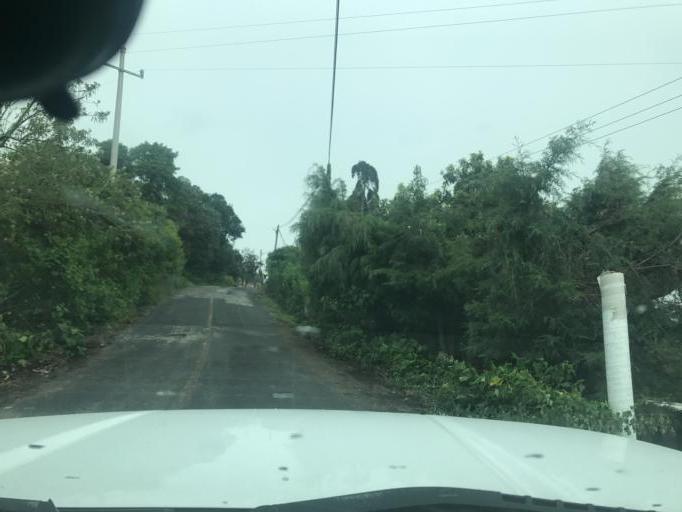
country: MX
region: Morelos
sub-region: Ocuituco
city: Huepalcalco (San Miguel)
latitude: 18.8998
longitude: -98.7536
